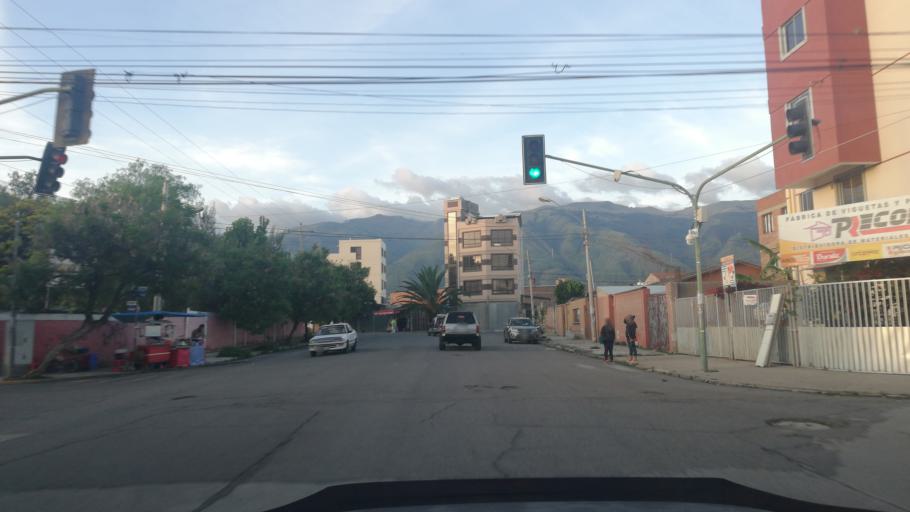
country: BO
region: Cochabamba
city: Cochabamba
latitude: -17.3742
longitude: -66.1872
